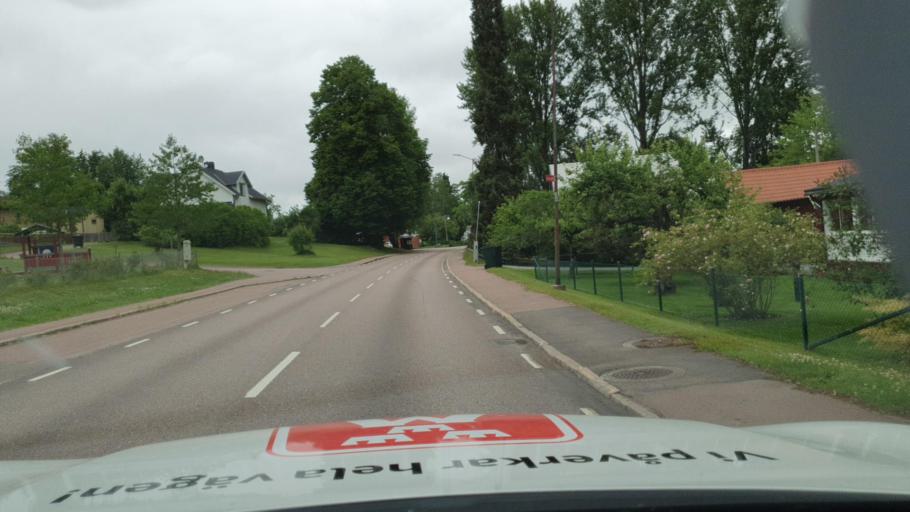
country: SE
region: Vaermland
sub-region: Karlstads Kommun
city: Edsvalla
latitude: 59.4344
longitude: 13.2113
